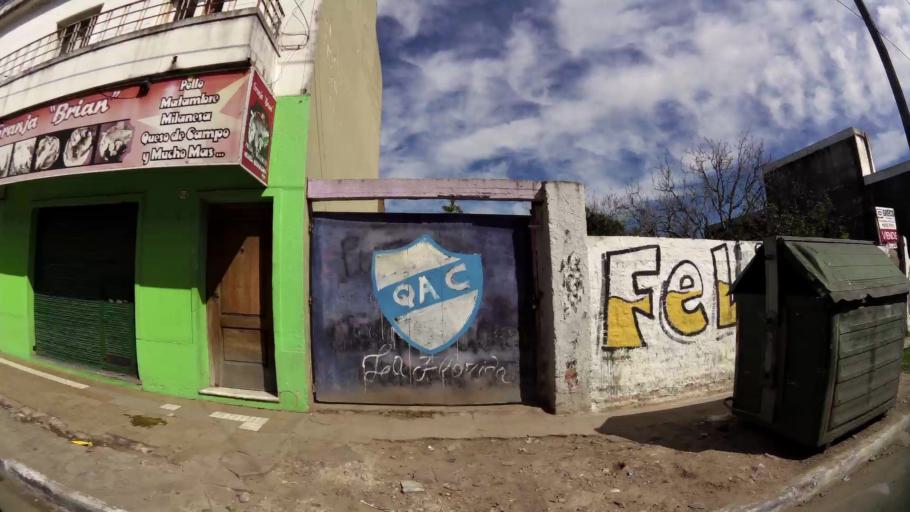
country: AR
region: Buenos Aires
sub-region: Partido de Quilmes
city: Quilmes
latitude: -34.7707
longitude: -58.2957
